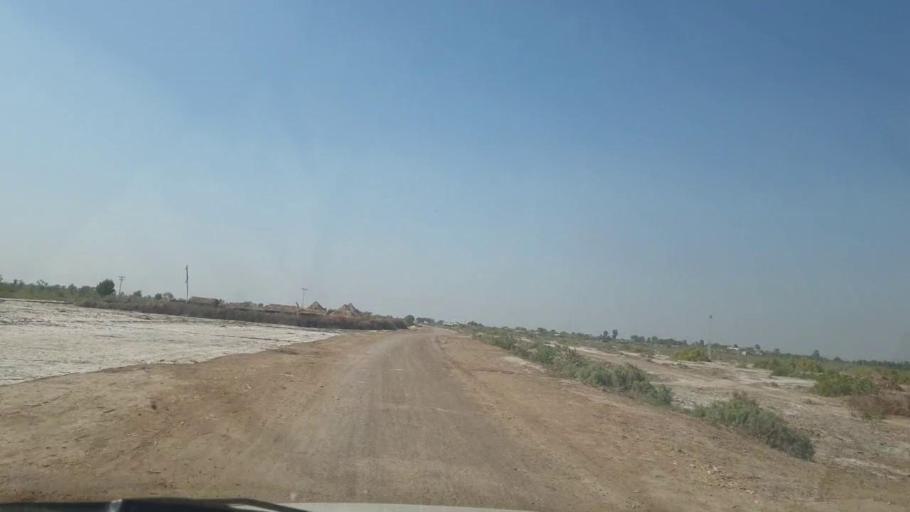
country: PK
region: Sindh
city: Mirpur Khas
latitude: 25.4746
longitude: 69.1226
